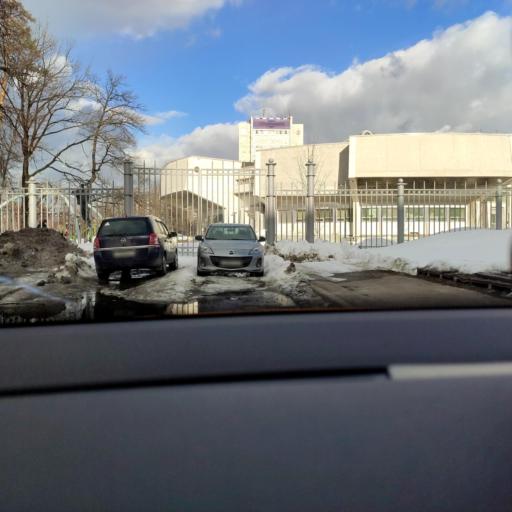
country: RU
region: Moscow
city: Vatutino
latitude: 55.8568
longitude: 37.6880
